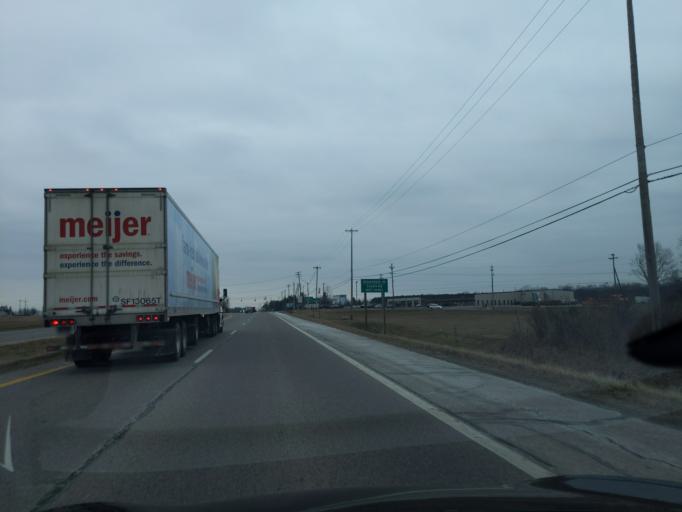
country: US
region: Michigan
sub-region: Eaton County
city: Dimondale
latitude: 42.6829
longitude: -84.6443
